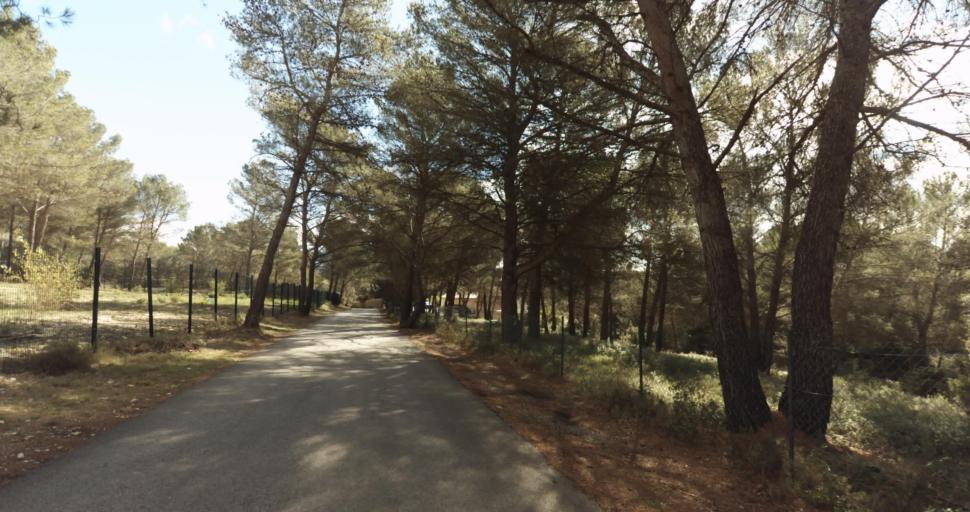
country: FR
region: Provence-Alpes-Cote d'Azur
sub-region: Departement des Bouches-du-Rhone
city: Venelles
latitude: 43.5936
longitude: 5.4953
